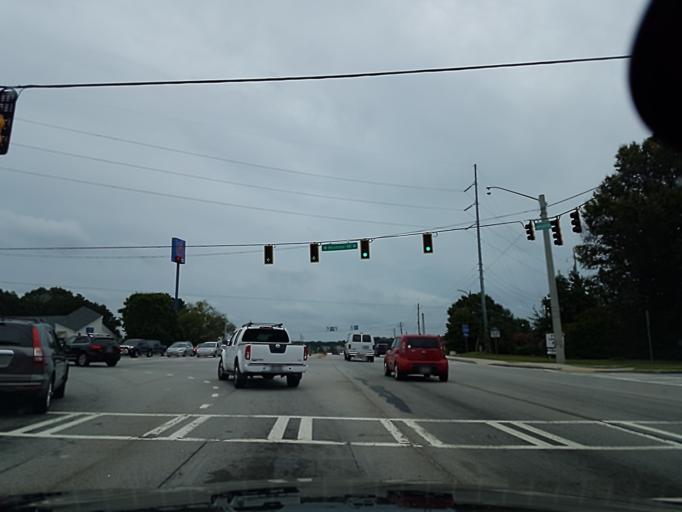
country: US
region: Georgia
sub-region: DeKalb County
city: Clarkston
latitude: 33.8259
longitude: -84.2563
